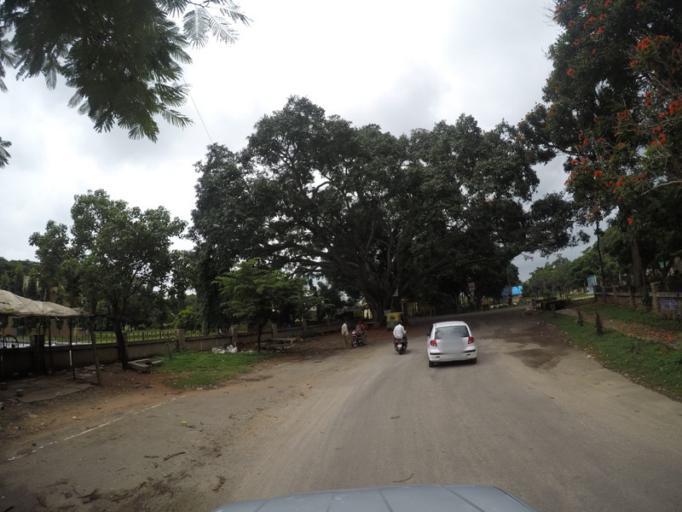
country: IN
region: Karnataka
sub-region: Bangalore Rural
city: Nelamangala
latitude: 13.1355
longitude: 77.4914
